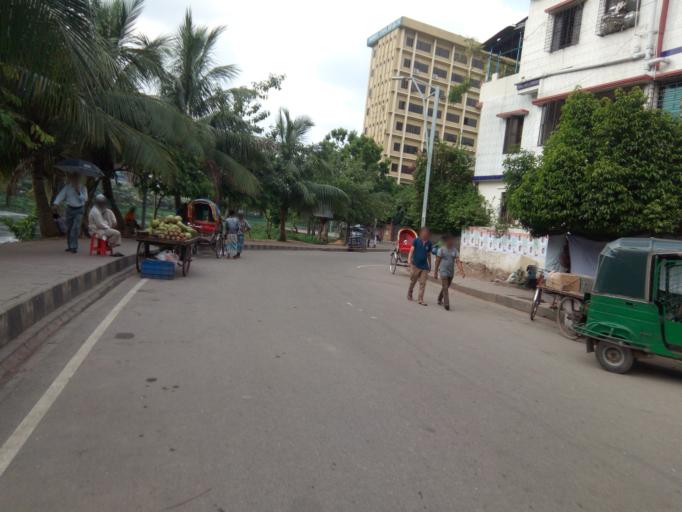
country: BD
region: Dhaka
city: Azimpur
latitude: 23.7479
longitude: 90.3958
